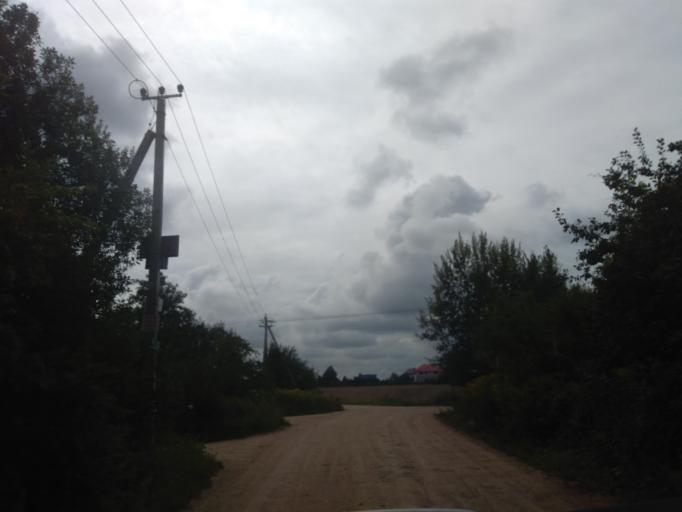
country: BY
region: Minsk
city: Slabada
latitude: 53.9864
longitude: 27.9129
